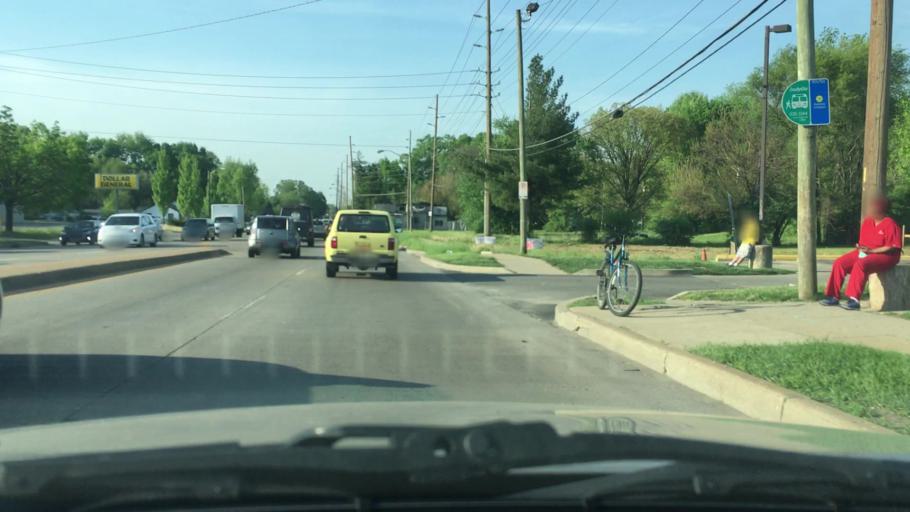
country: US
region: Indiana
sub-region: Marion County
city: Broad Ripple
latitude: 39.8250
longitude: -86.1219
